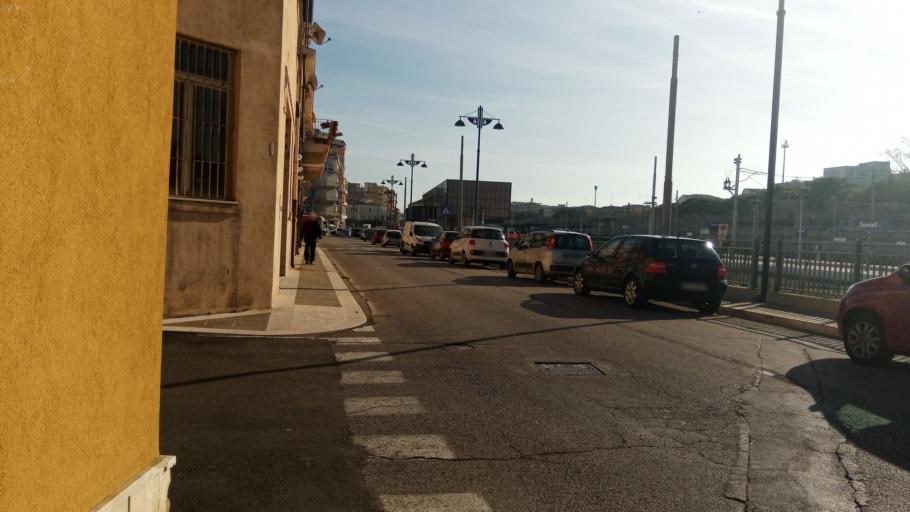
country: IT
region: Molise
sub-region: Provincia di Campobasso
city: Termoli
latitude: 42.0029
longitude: 14.9907
